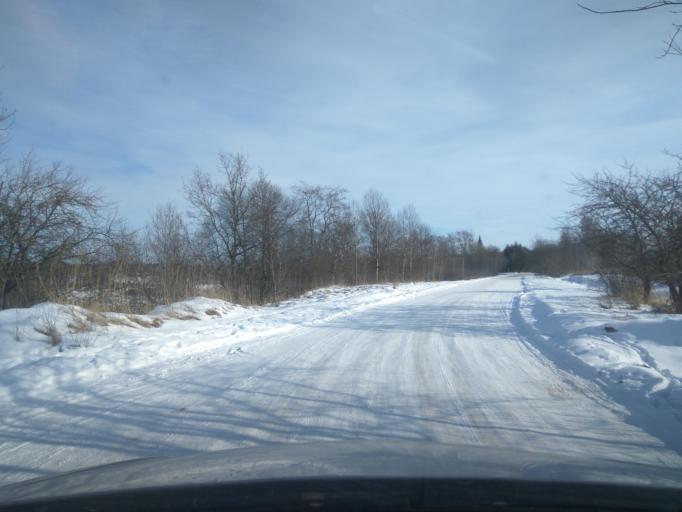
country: LV
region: Kuldigas Rajons
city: Kuldiga
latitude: 56.9821
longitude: 21.9565
